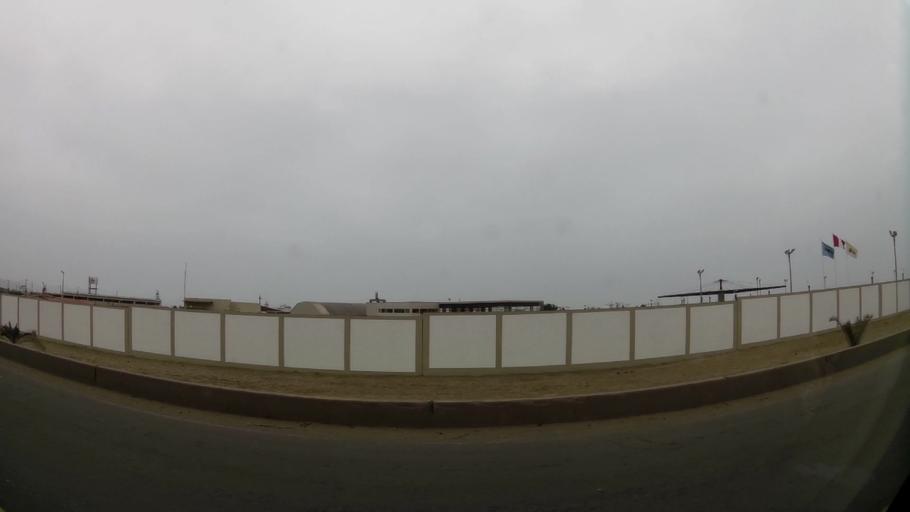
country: PE
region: Lima
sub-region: Lima
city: Punta Hermosa
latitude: -12.3229
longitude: -76.8280
